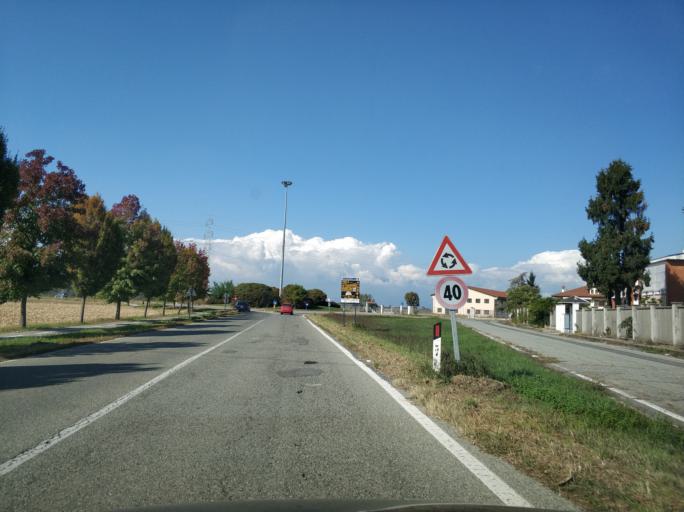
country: IT
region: Piedmont
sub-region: Provincia di Torino
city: Borgaro Torinese
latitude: 45.1511
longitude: 7.6754
